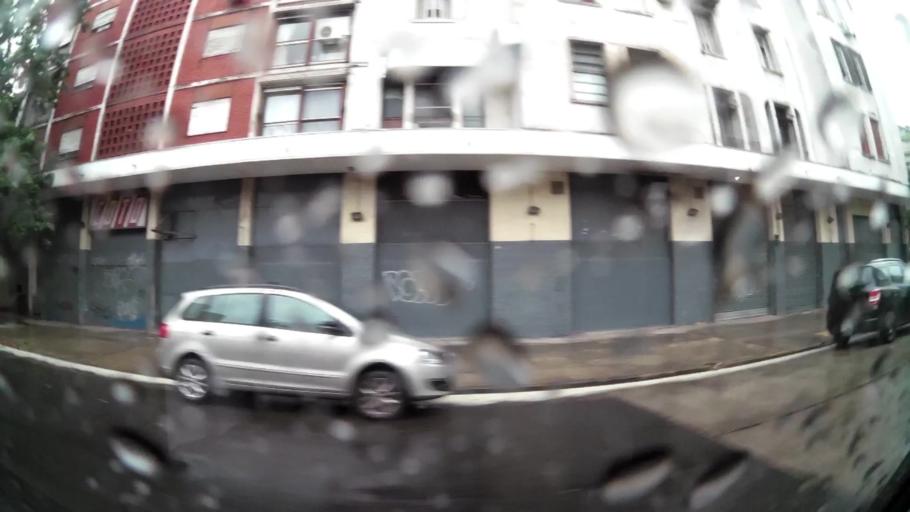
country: AR
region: Buenos Aires F.D.
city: Buenos Aires
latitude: -34.6301
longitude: -58.3719
